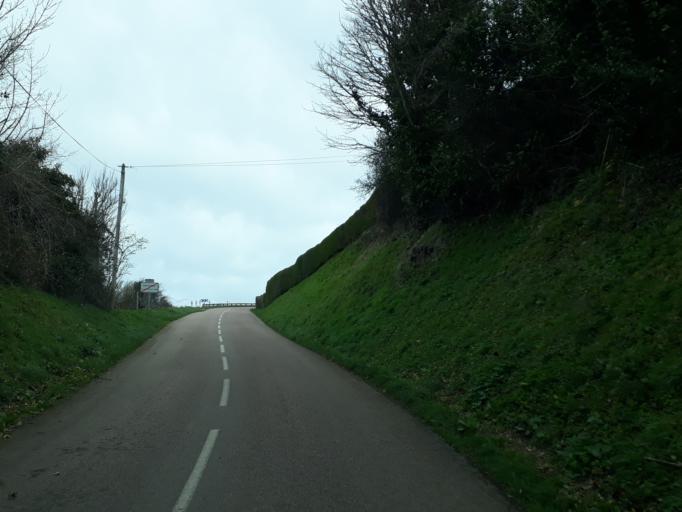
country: FR
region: Haute-Normandie
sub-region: Departement de la Seine-Maritime
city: Yport
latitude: 49.7374
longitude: 0.2934
